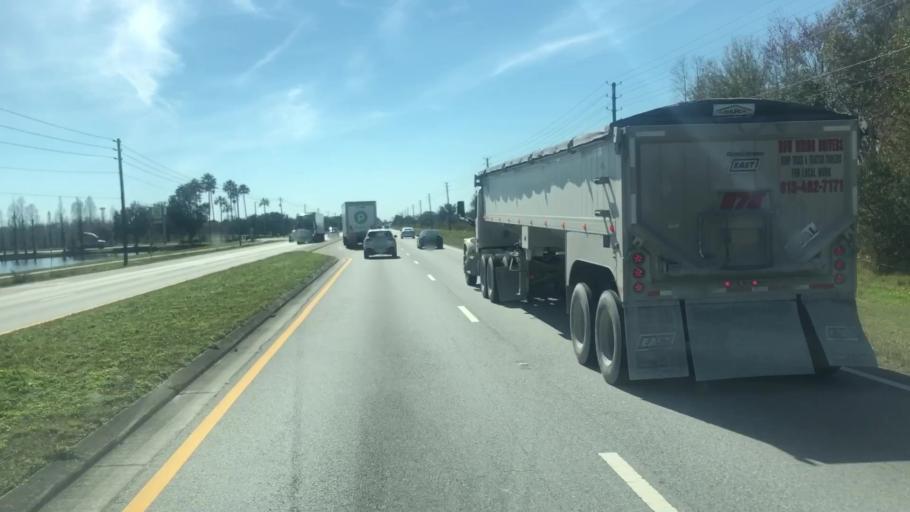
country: US
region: Florida
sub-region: Polk County
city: Winston
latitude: 28.0160
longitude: -82.0557
